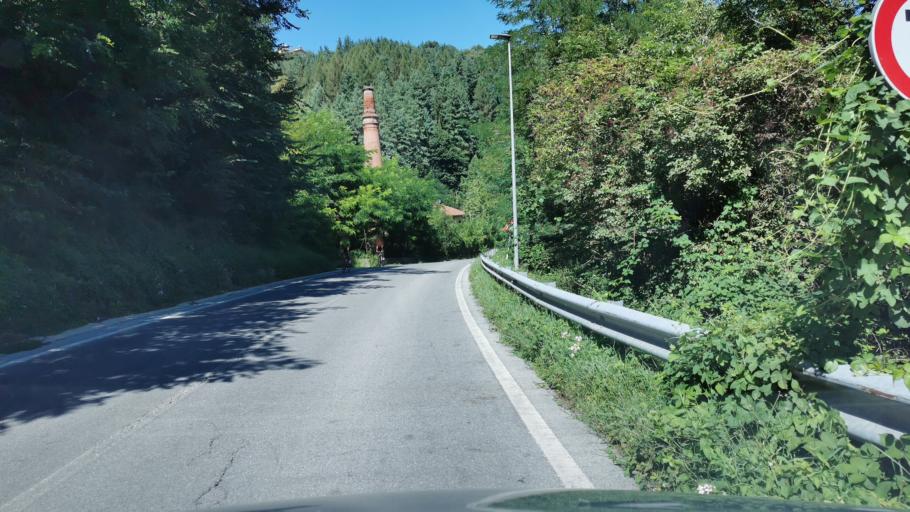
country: IT
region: Piedmont
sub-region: Provincia di Cuneo
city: Roccavione
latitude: 44.3199
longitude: 7.4687
